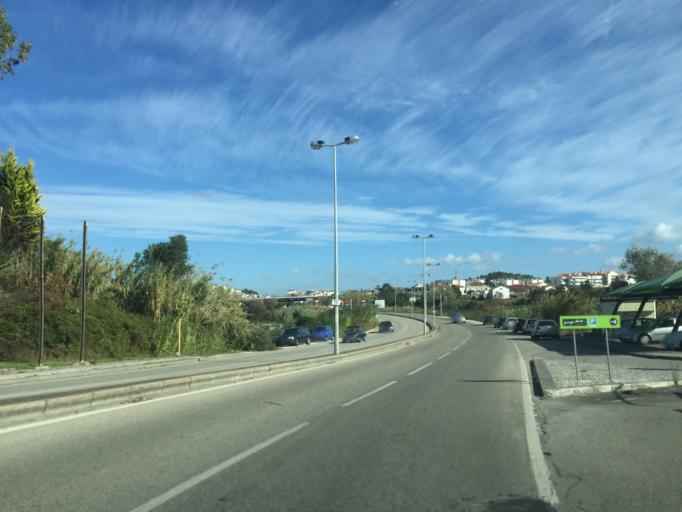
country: PT
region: Coimbra
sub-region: Figueira da Foz
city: Tavarede
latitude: 40.1635
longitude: -8.8478
